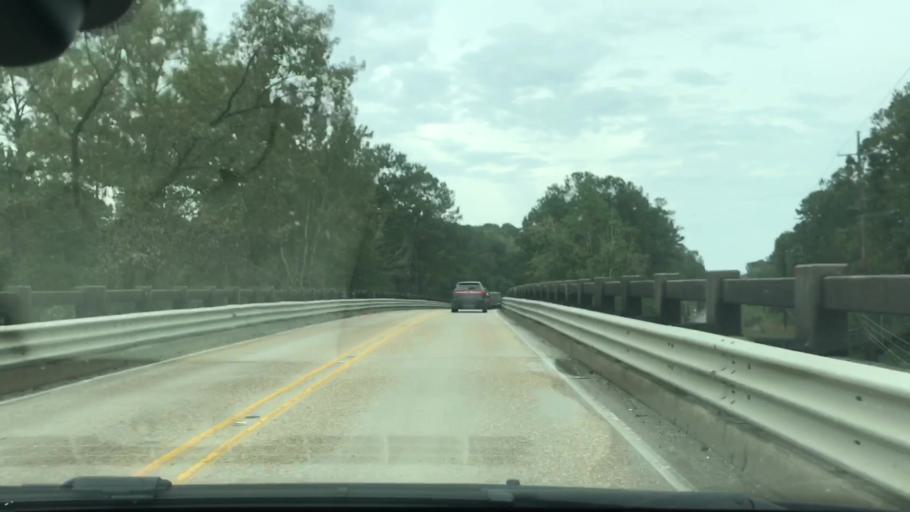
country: US
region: Louisiana
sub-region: Saint Tammany Parish
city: Slidell
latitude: 30.2947
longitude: -89.7764
